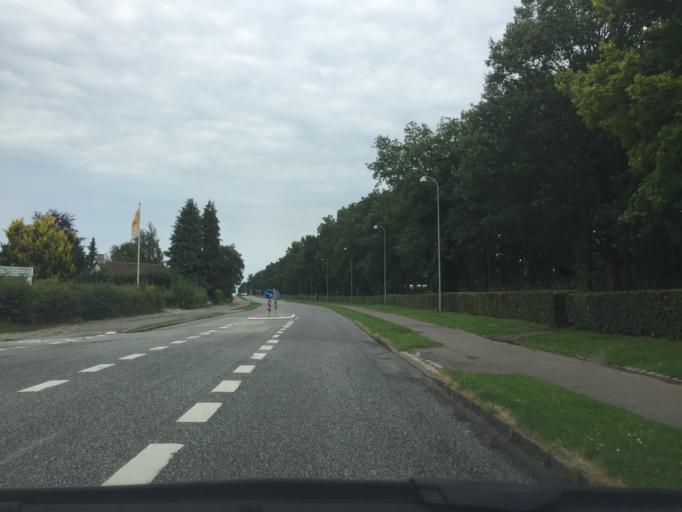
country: DK
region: Capital Region
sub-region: Lyngby-Tarbaek Kommune
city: Kongens Lyngby
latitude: 55.7886
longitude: 12.5174
